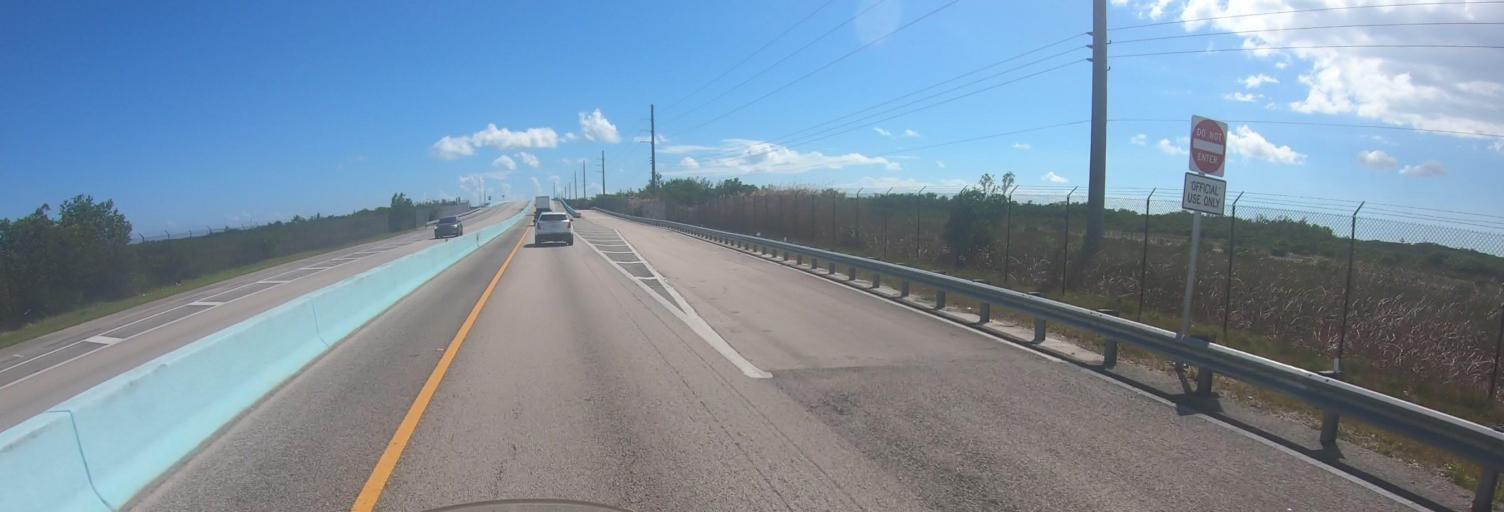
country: US
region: Florida
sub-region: Monroe County
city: North Key Largo
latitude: 25.2936
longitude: -80.4458
